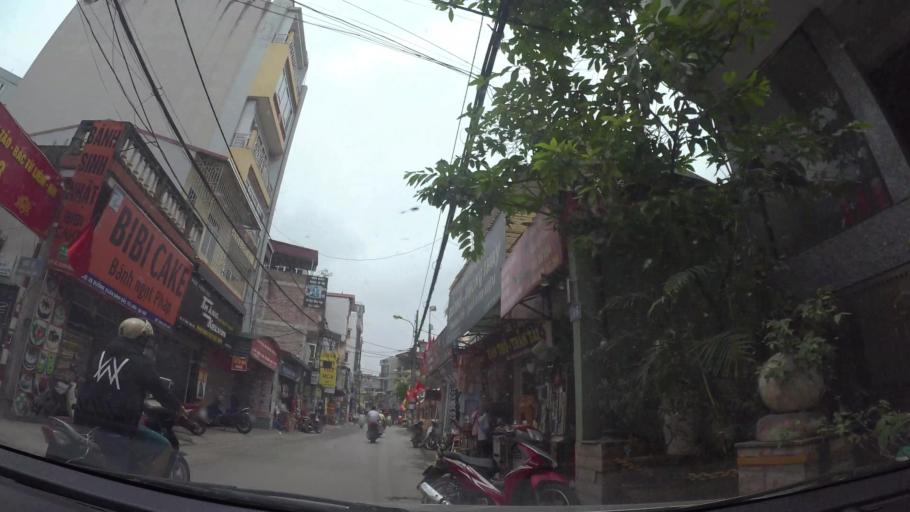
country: VN
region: Ha Noi
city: Tay Ho
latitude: 21.0698
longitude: 105.8018
